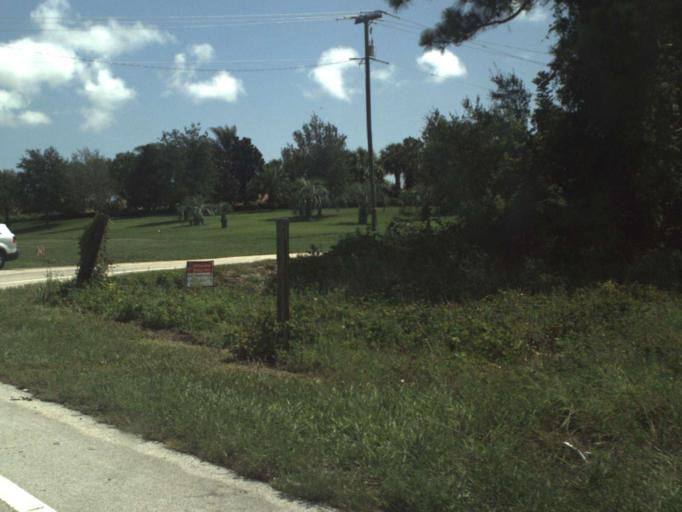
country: US
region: Florida
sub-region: Indian River County
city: Gifford
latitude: 27.6823
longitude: -80.4462
